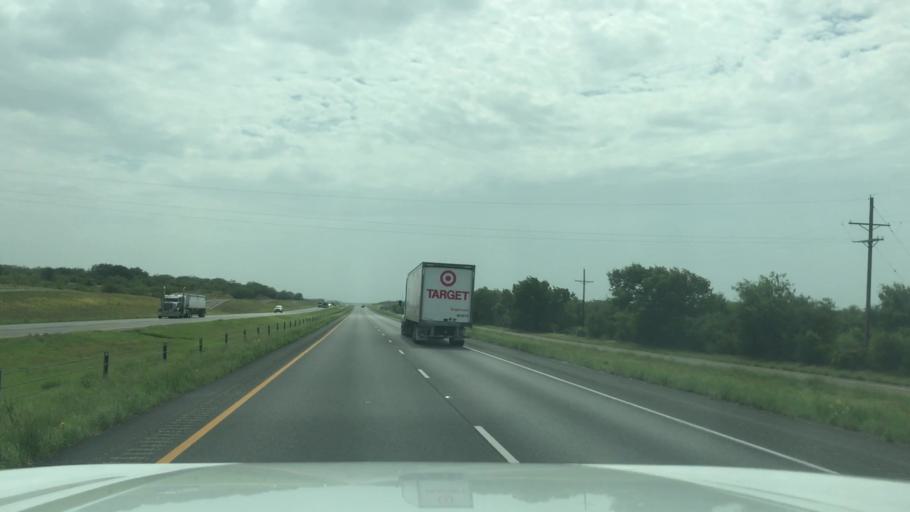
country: US
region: Texas
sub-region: Callahan County
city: Baird
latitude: 32.3840
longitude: -99.2863
